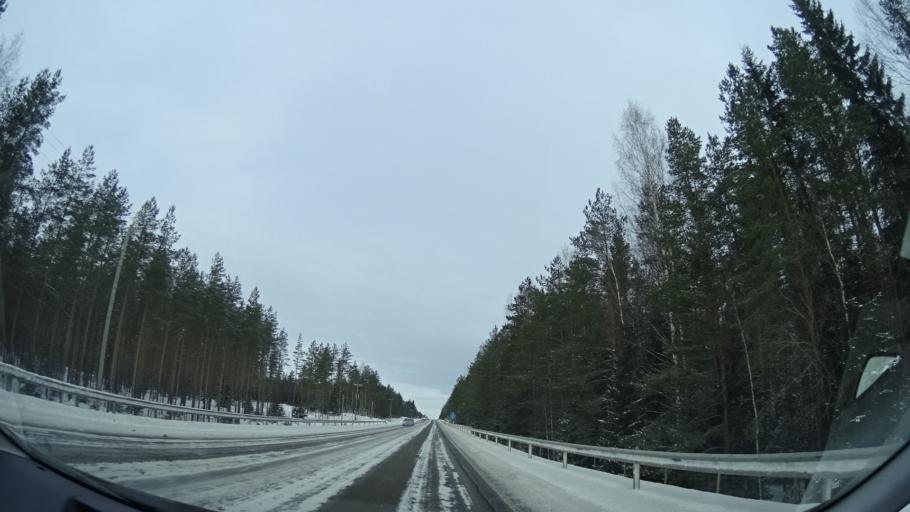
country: FI
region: Uusimaa
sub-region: Helsinki
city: Kaerkoelae
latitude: 60.6551
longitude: 23.8564
